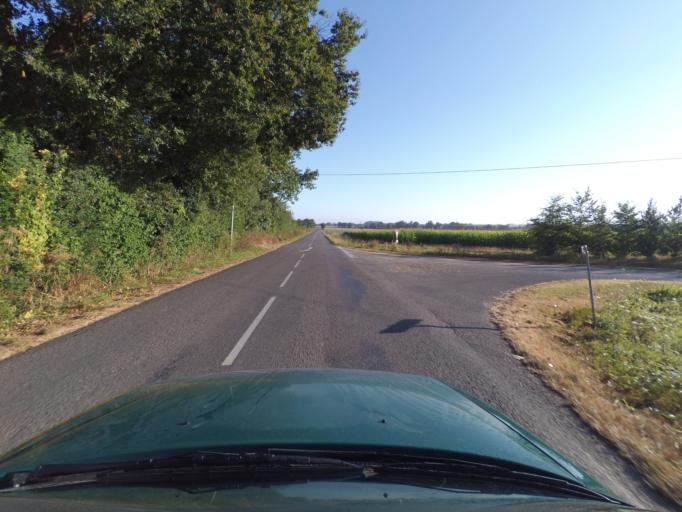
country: FR
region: Pays de la Loire
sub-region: Departement de la Loire-Atlantique
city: La Planche
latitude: 46.9995
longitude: -1.4553
